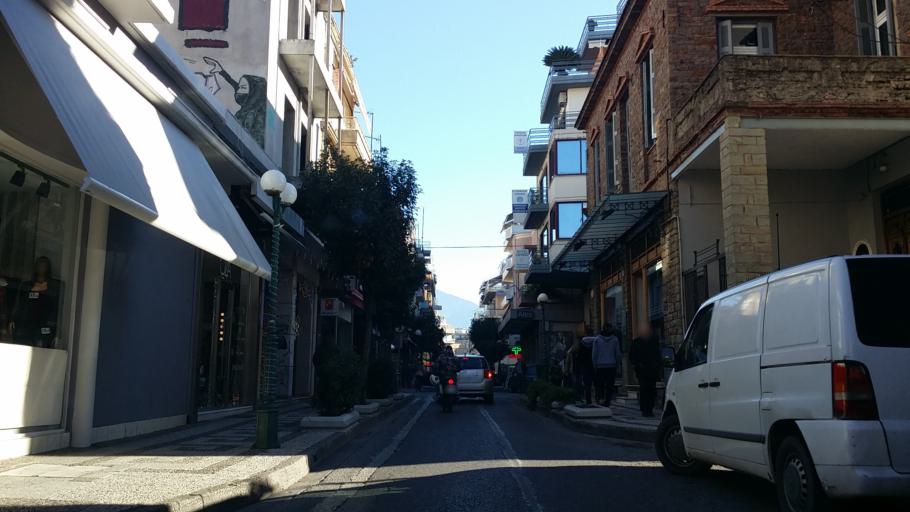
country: GR
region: West Greece
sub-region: Nomos Aitolias kai Akarnanias
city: Agrinio
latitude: 38.6248
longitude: 21.4111
